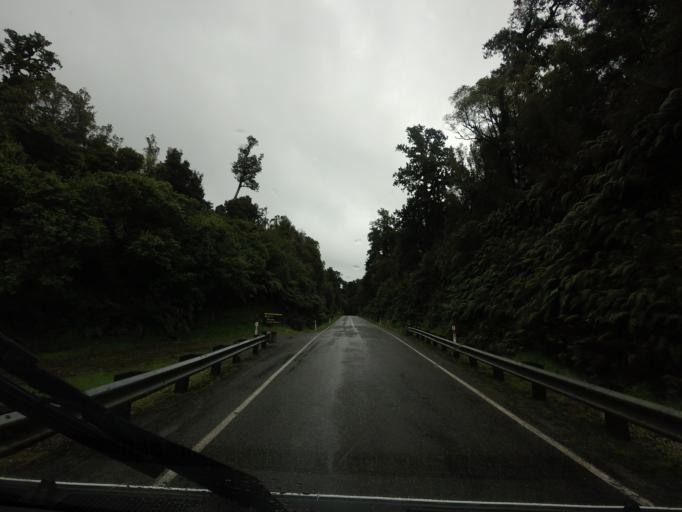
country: NZ
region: West Coast
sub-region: Westland District
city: Hokitika
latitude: -42.9811
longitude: 170.6836
